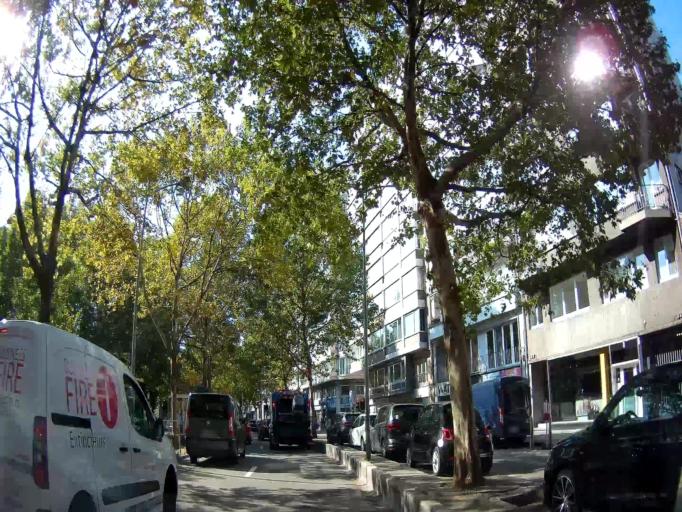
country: BE
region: Wallonia
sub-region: Province de Liege
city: Liege
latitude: 50.6376
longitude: 5.5677
